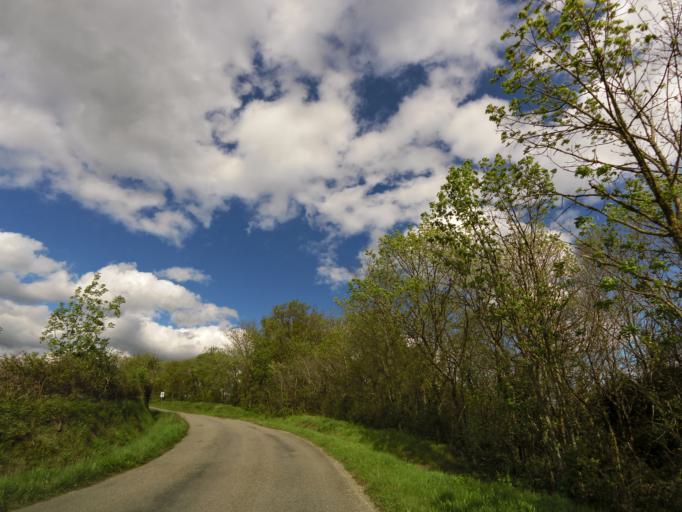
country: FR
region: Languedoc-Roussillon
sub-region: Departement de l'Aude
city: Saint-Martin-Lalande
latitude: 43.3636
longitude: 2.0563
